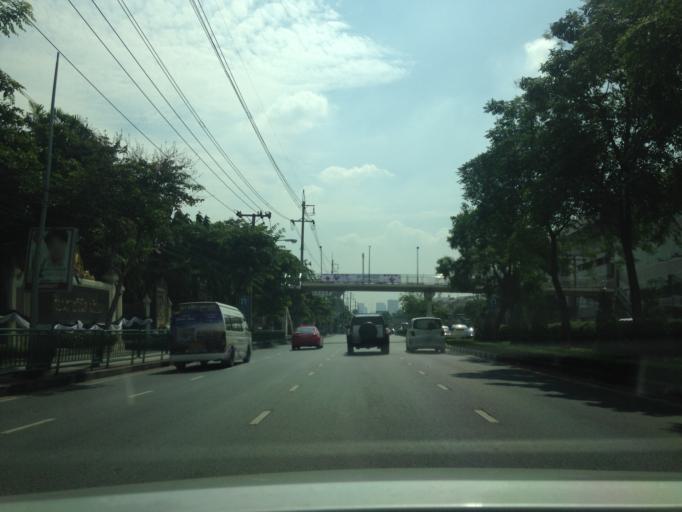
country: TH
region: Bangkok
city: Pom Prap Sattru Phai
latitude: 13.7628
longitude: 100.5143
